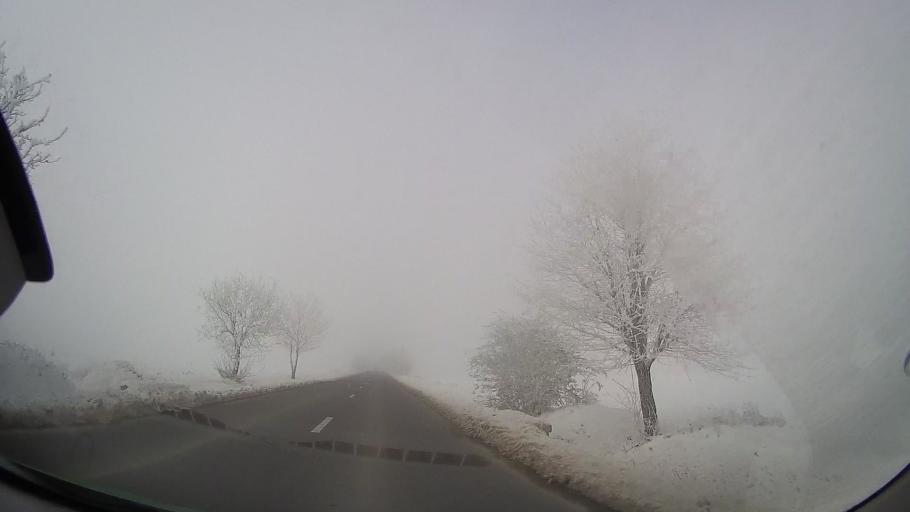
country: RO
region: Iasi
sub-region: Comuna Stolniceni-Prajescu
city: Stolniceni-Prajescu
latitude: 47.1855
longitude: 26.7407
